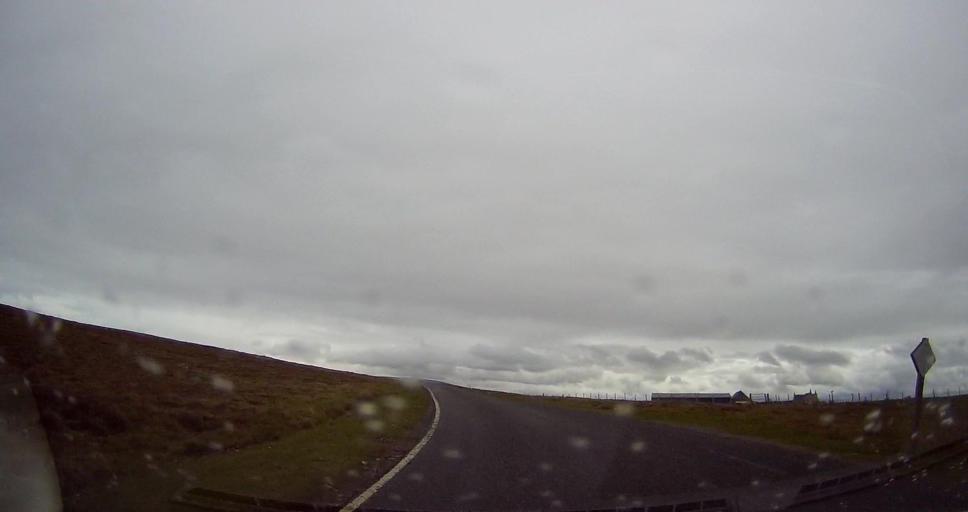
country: GB
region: Scotland
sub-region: Shetland Islands
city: Lerwick
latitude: 60.4865
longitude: -1.6040
